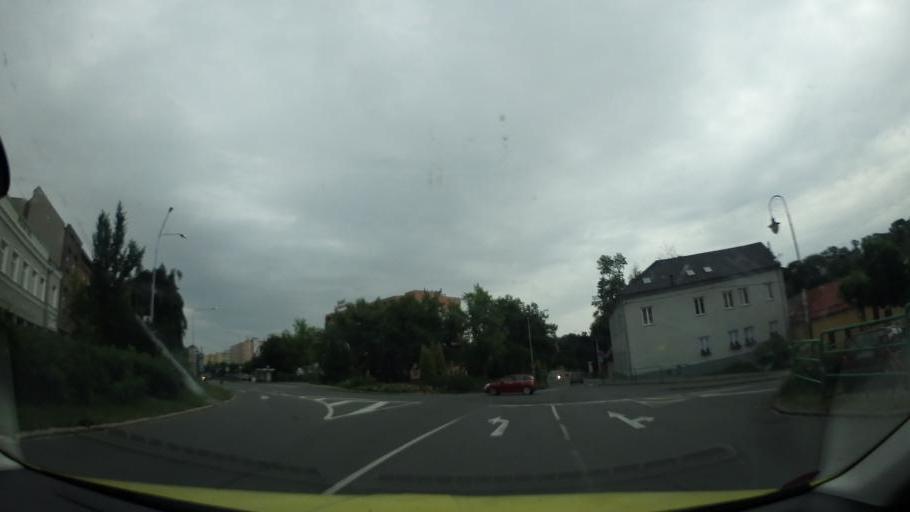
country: CZ
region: Olomoucky
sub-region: Okres Prerov
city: Hranice
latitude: 49.5513
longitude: 17.7350
